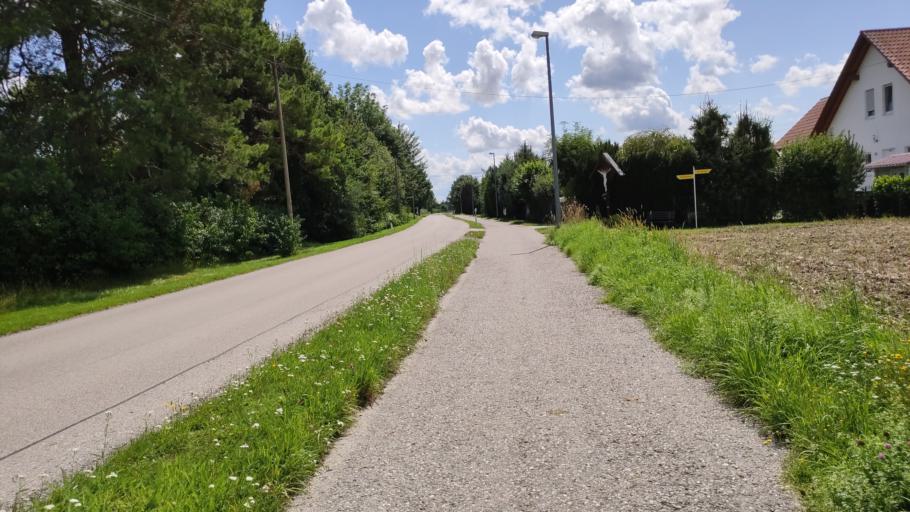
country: DE
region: Bavaria
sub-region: Swabia
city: Konigsbrunn
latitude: 48.2413
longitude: 10.8932
